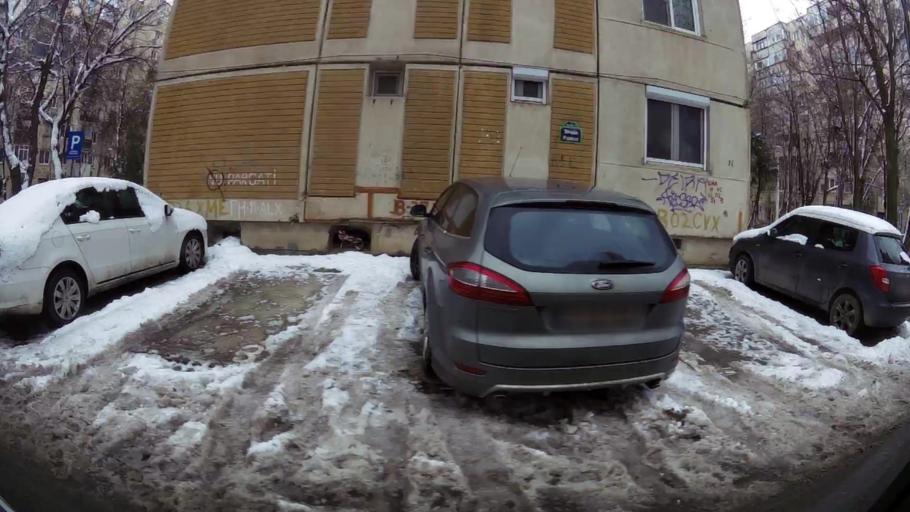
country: RO
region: Bucuresti
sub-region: Municipiul Bucuresti
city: Bucuresti
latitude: 44.3992
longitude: 26.1040
